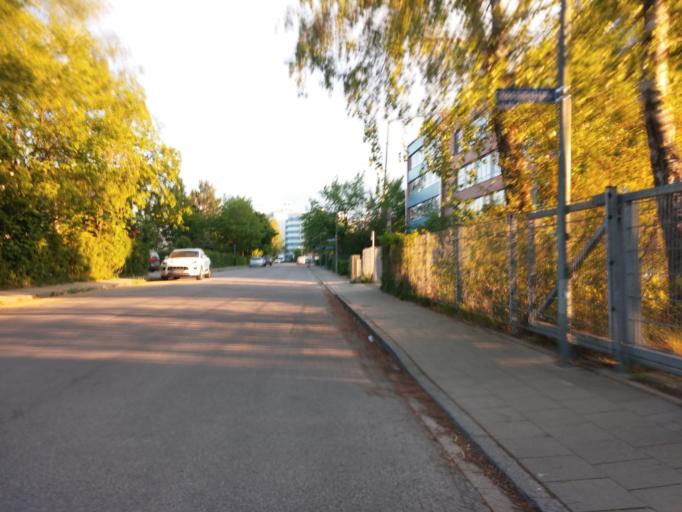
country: DE
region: Bavaria
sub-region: Upper Bavaria
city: Vaterstetten
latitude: 48.1067
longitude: 11.7878
